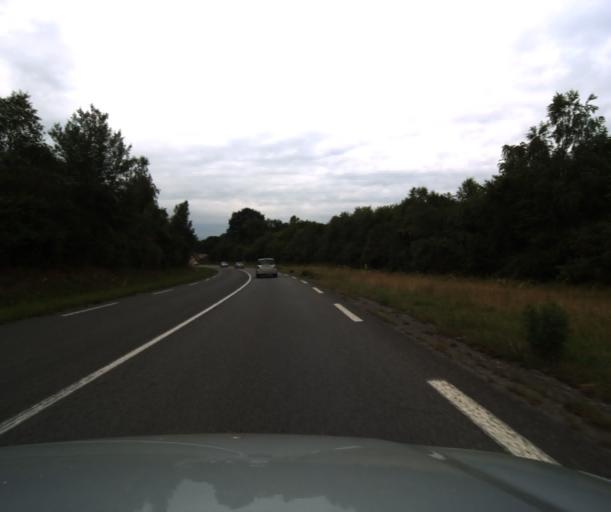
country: FR
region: Midi-Pyrenees
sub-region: Departement des Hautes-Pyrenees
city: Juillan
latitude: 43.1875
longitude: 0.0091
